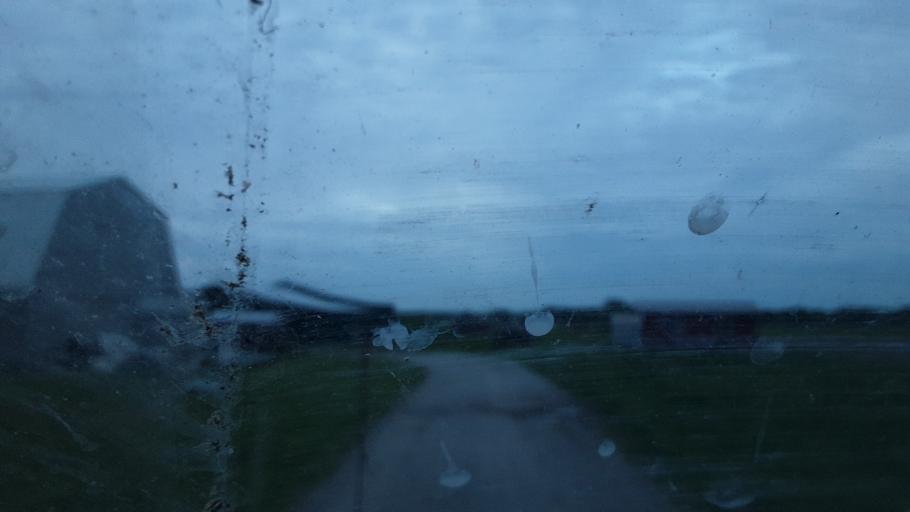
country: US
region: Missouri
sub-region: Clark County
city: Kahoka
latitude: 40.4389
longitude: -91.6057
